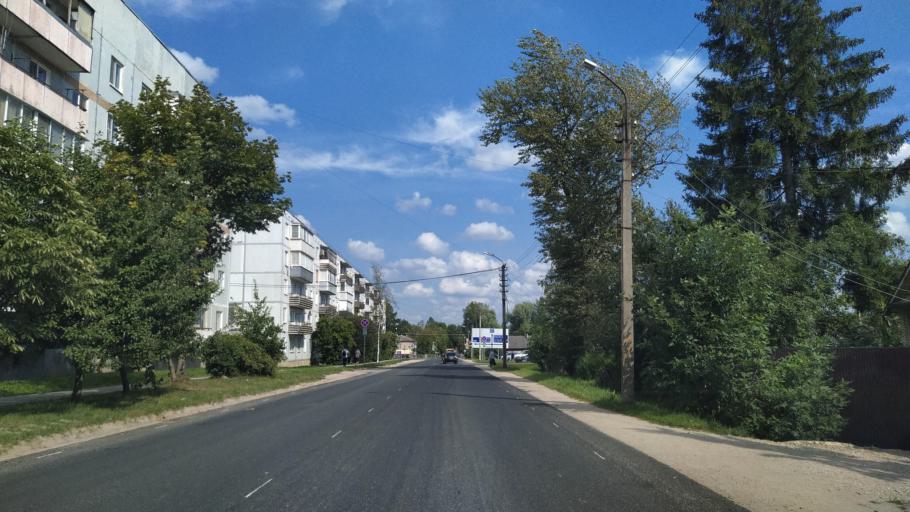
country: RU
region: Pskov
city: Porkhov
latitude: 57.7609
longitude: 29.5530
